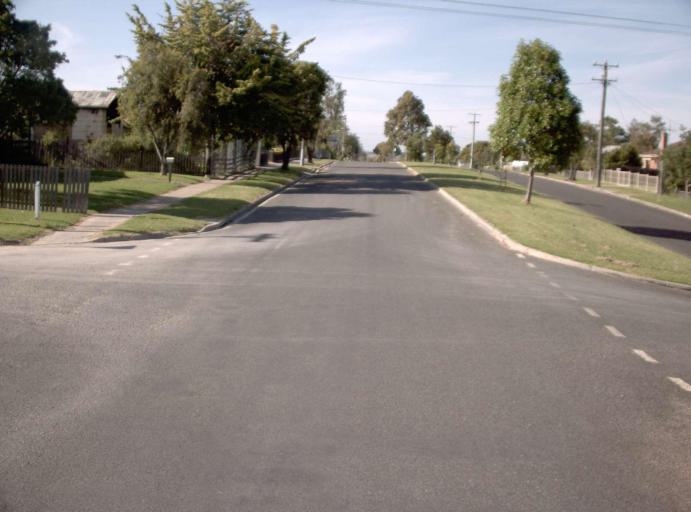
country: AU
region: Victoria
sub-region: East Gippsland
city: Lakes Entrance
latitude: -37.6955
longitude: 148.4577
